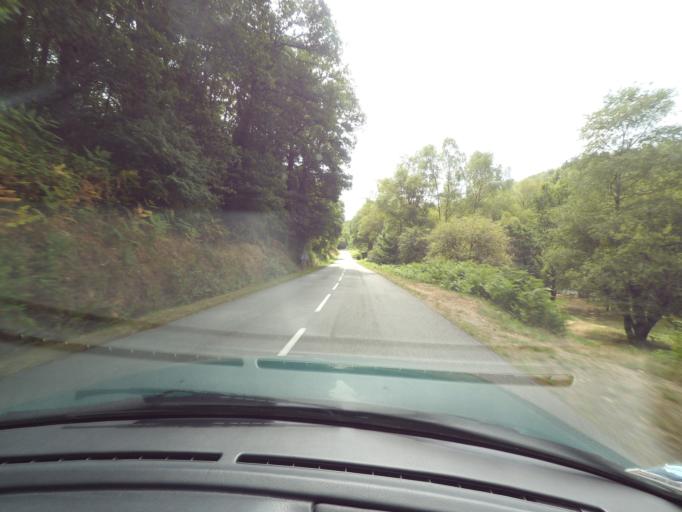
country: FR
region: Limousin
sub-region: Departement de la Haute-Vienne
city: Eymoutiers
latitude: 45.7146
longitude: 1.8429
